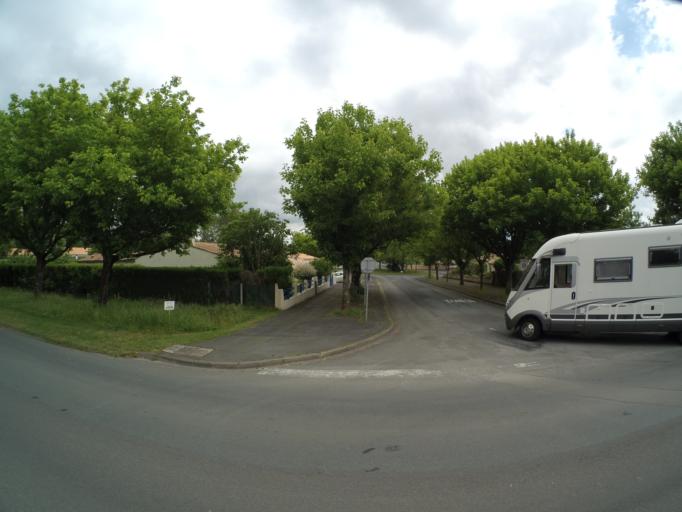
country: FR
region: Poitou-Charentes
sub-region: Departement de la Charente-Maritime
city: Breuil-Magne
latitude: 45.9620
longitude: -0.9698
